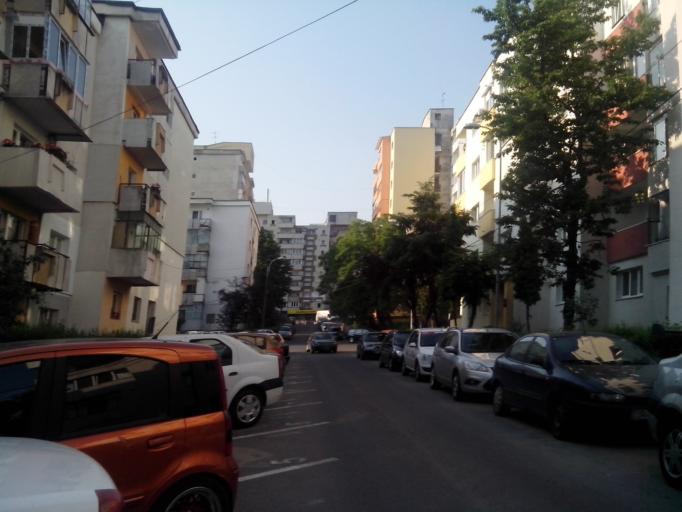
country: RO
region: Cluj
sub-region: Comuna Baciu
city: Baciu
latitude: 46.7592
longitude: 23.5459
